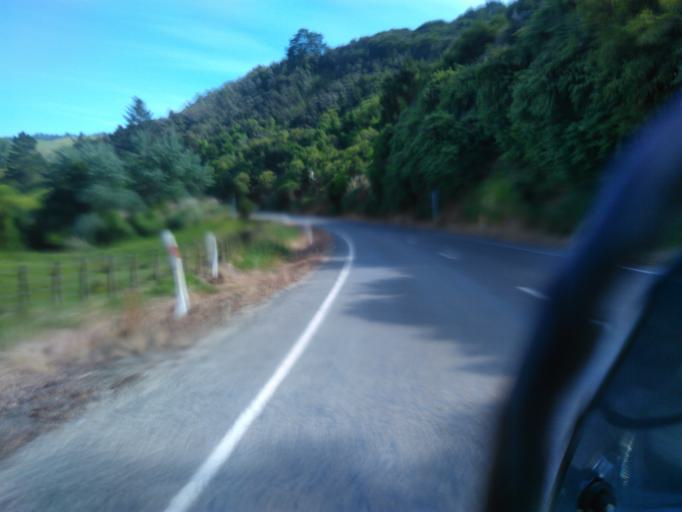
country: NZ
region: Hawke's Bay
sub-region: Wairoa District
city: Wairoa
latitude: -38.8659
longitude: 177.1991
